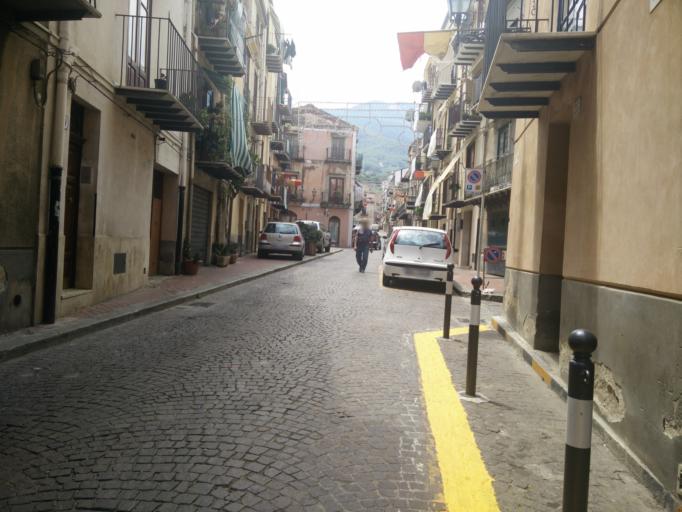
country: IT
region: Sicily
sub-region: Palermo
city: Castelbuono
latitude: 37.9320
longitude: 14.0870
